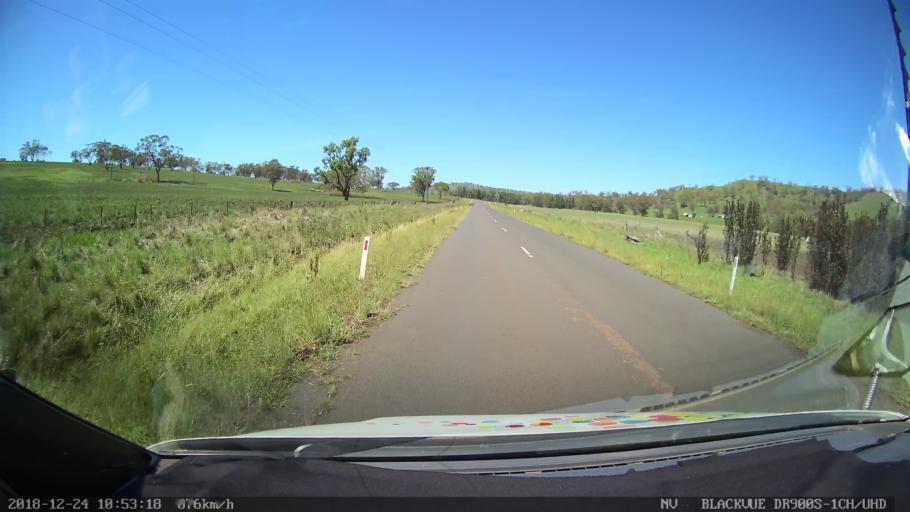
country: AU
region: New South Wales
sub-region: Upper Hunter Shire
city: Merriwa
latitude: -31.9902
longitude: 150.4219
